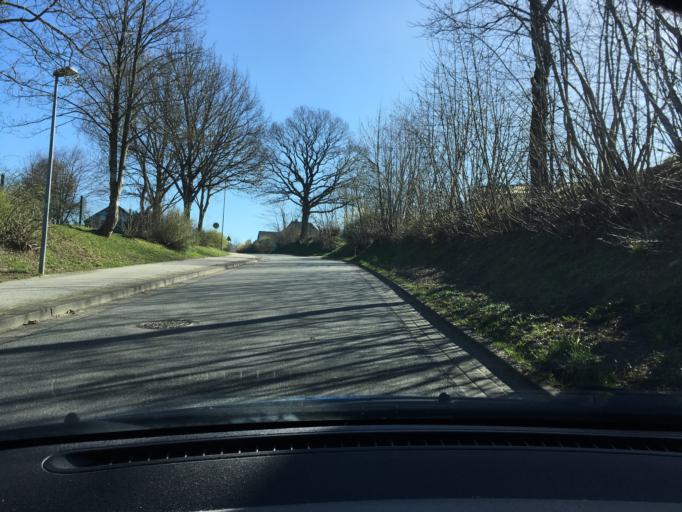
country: DE
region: Schleswig-Holstein
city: Fahrdorf
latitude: 54.5043
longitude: 9.6077
